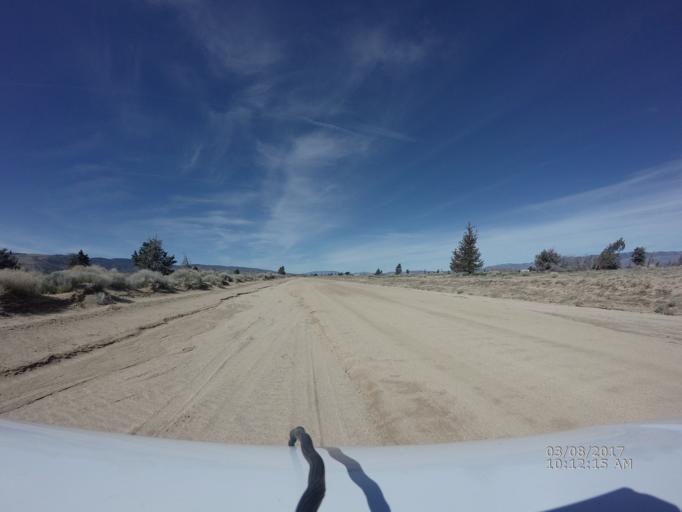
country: US
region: California
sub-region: Los Angeles County
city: Green Valley
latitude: 34.7531
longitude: -118.4527
